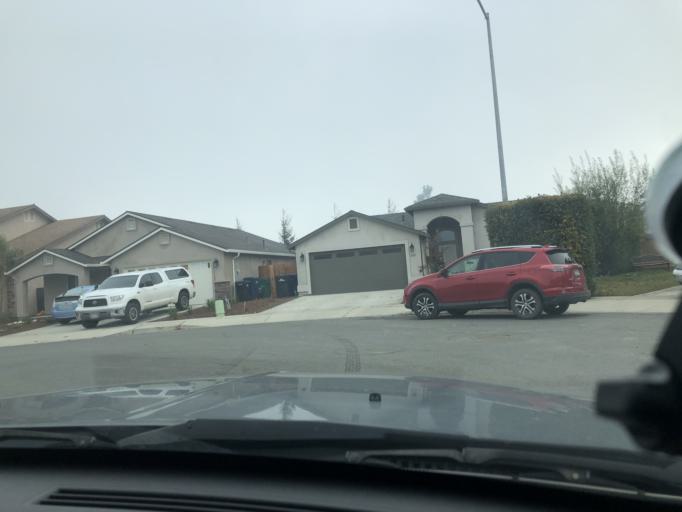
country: US
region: California
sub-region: Monterey County
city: King City
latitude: 36.2074
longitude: -121.1410
